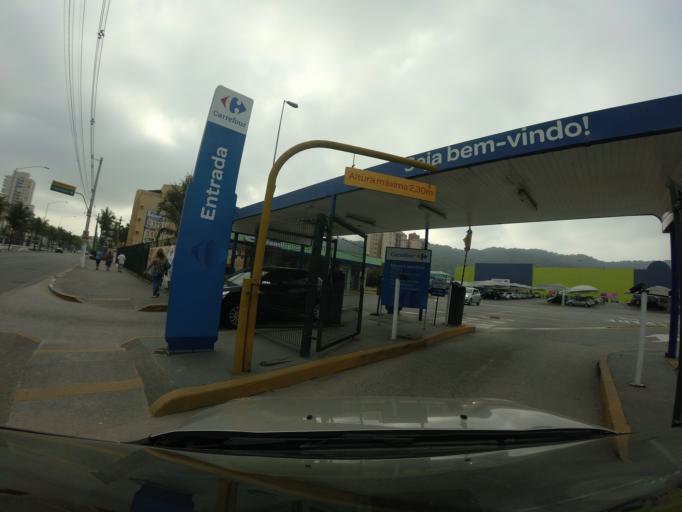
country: BR
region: Sao Paulo
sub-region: Guaruja
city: Guaruja
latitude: -23.9820
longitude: -46.2314
